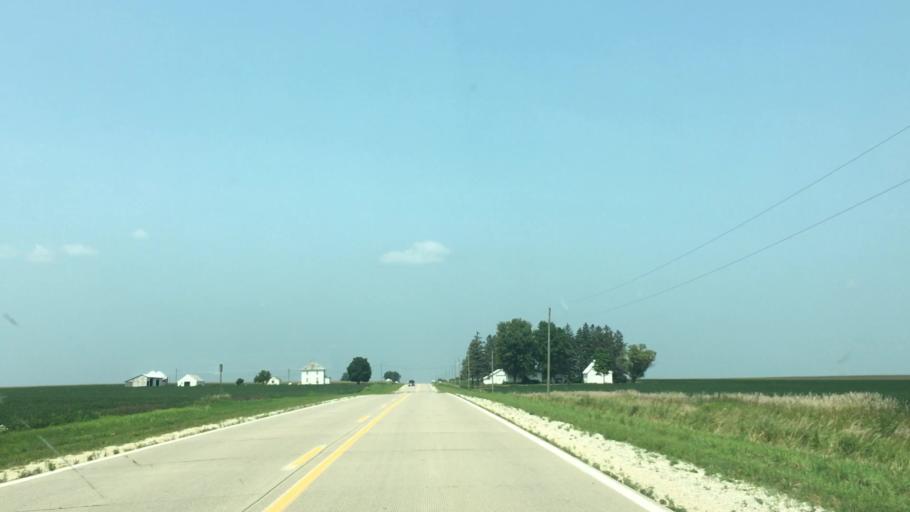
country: US
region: Iowa
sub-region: Fayette County
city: Oelwein
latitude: 42.7081
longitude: -91.8048
